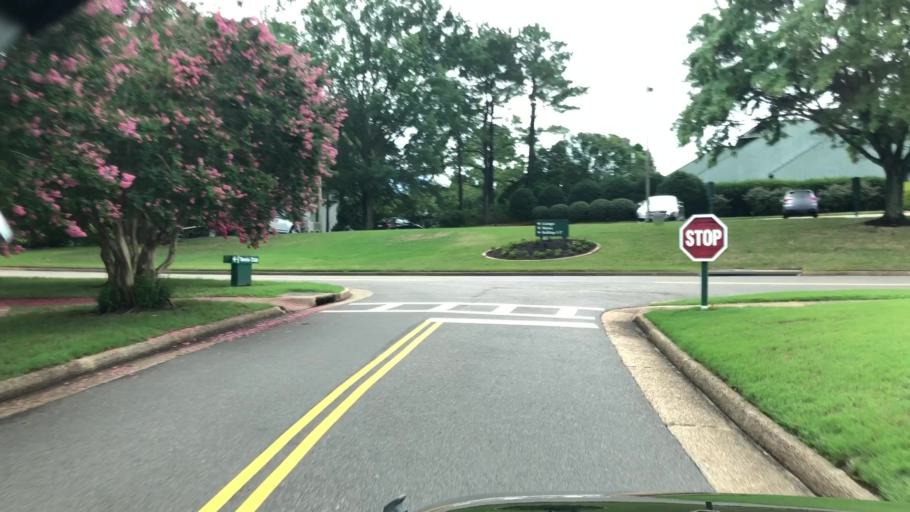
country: US
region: Virginia
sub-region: City of Williamsburg
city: Williamsburg
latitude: 37.2255
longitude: -76.6652
